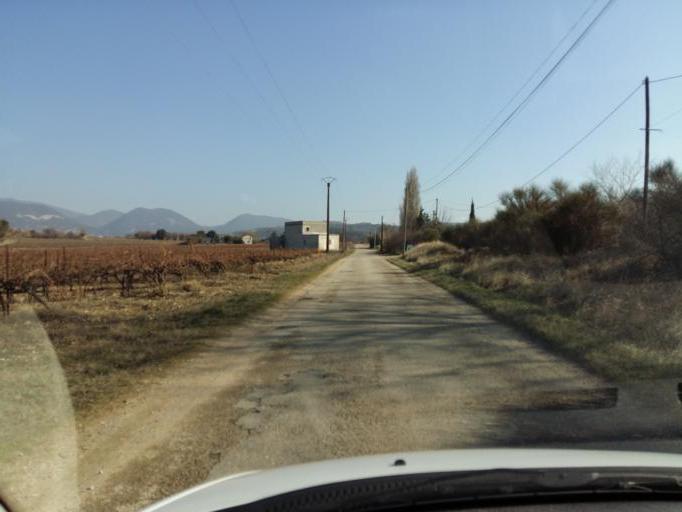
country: FR
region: Provence-Alpes-Cote d'Azur
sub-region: Departement du Vaucluse
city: Valreas
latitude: 44.3855
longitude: 5.0136
